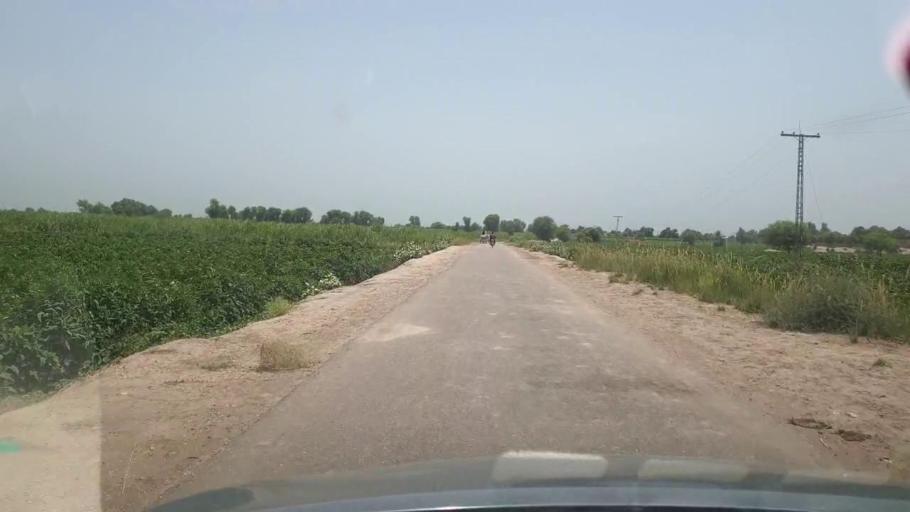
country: PK
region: Sindh
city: Hingorja
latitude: 27.2278
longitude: 68.3165
